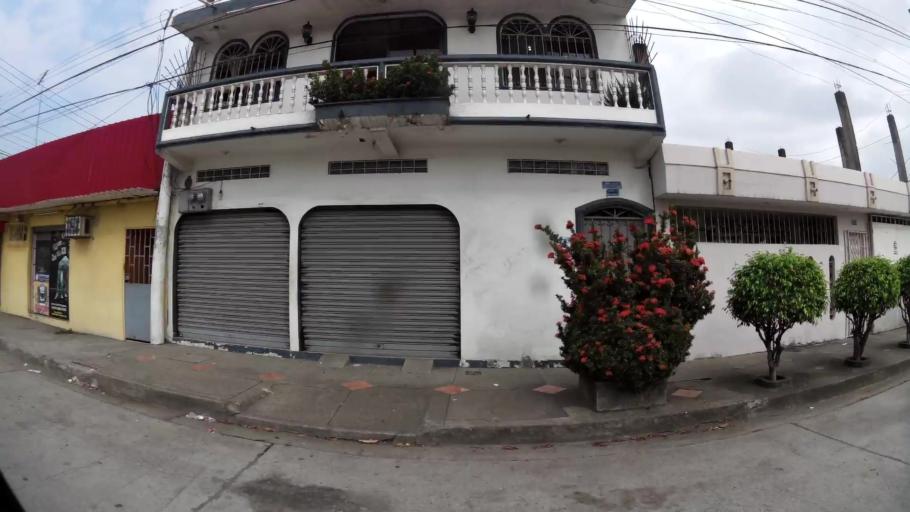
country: EC
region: Guayas
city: Eloy Alfaro
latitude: -2.1369
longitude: -79.8859
